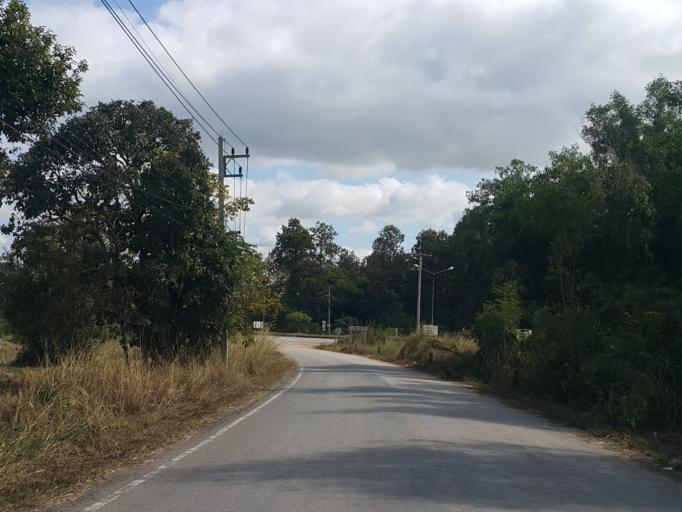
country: TH
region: Lampang
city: Hang Chat
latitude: 18.3280
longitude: 99.3895
